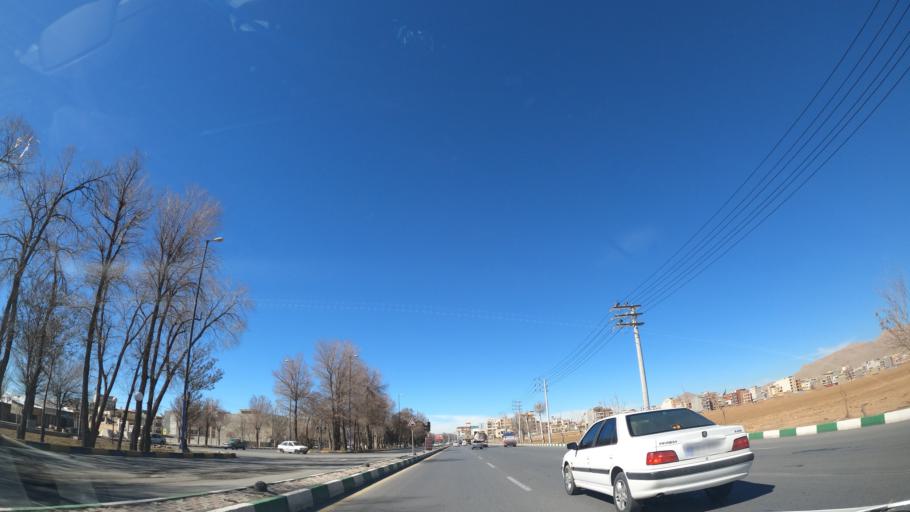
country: IR
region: Chahar Mahall va Bakhtiari
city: Shahrekord
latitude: 32.3098
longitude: 50.8930
